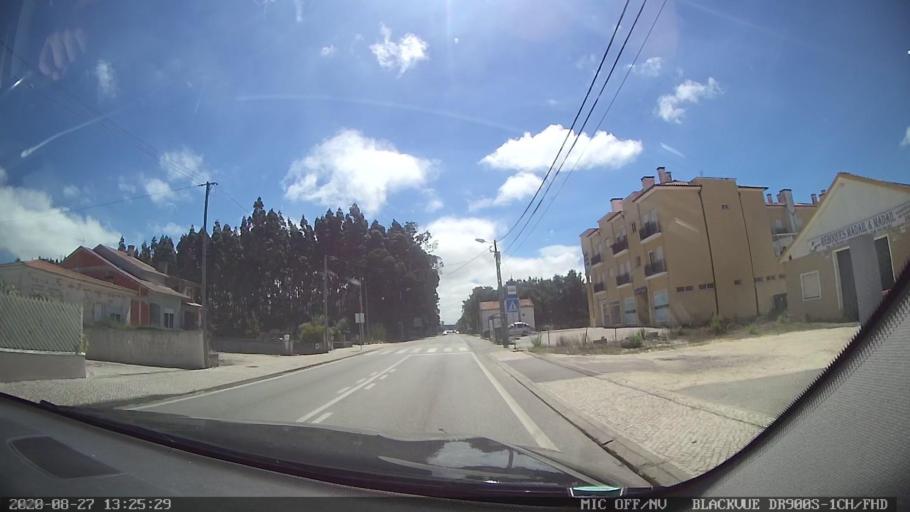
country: PT
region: Aveiro
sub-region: Vagos
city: Vagos
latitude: 40.5461
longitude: -8.6788
